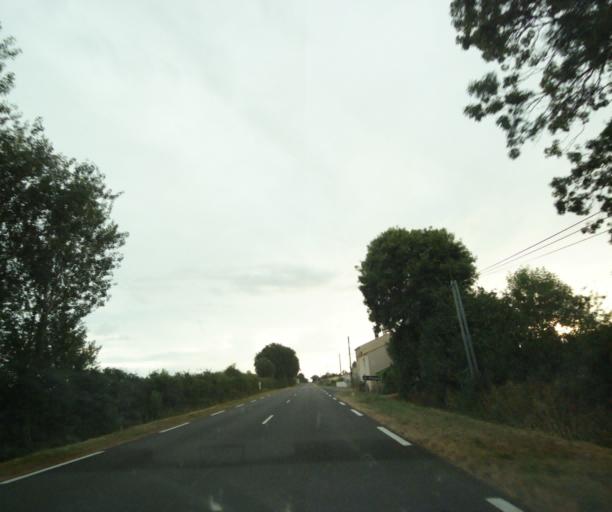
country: FR
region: Pays de la Loire
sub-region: Departement de la Vendee
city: Saint-Hilaire-de-Talmont
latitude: 46.4718
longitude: -1.5509
